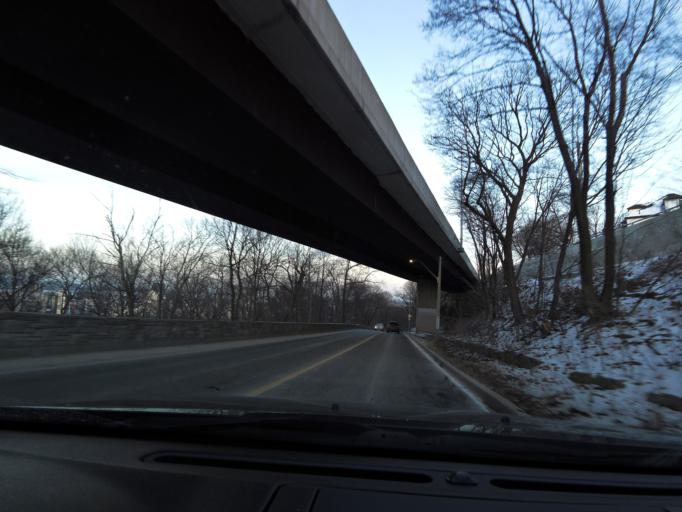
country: CA
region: Ontario
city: Hamilton
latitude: 43.2449
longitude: -79.8800
